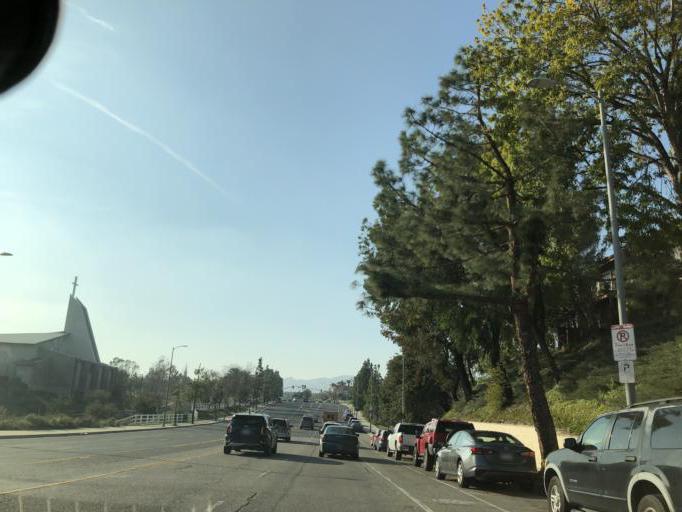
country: US
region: California
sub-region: Los Angeles County
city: Chatsworth
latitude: 34.2747
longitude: -118.5590
